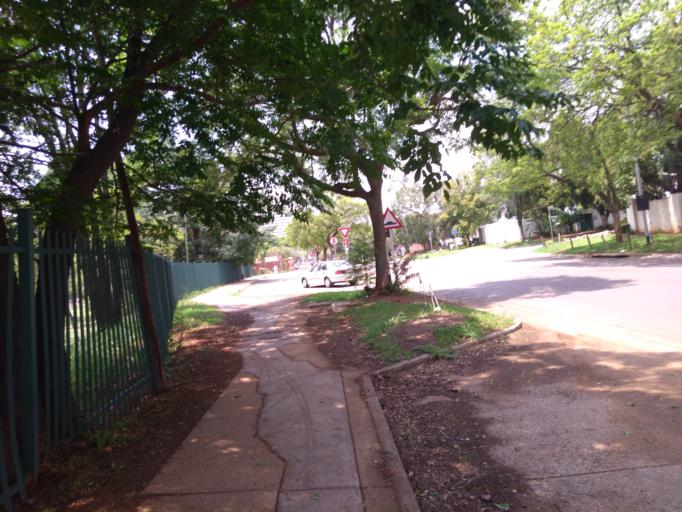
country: ZA
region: Gauteng
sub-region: City of Tshwane Metropolitan Municipality
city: Pretoria
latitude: -25.7600
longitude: 28.2304
